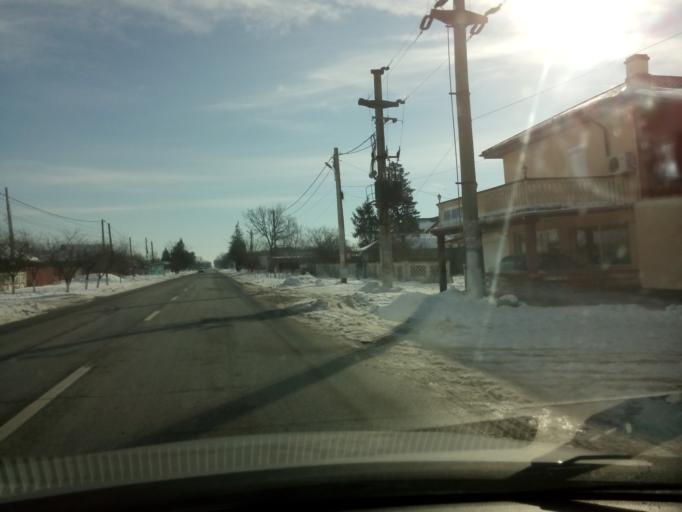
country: RO
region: Calarasi
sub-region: Comuna Frumusani
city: Frumusani
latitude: 44.2863
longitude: 26.3248
